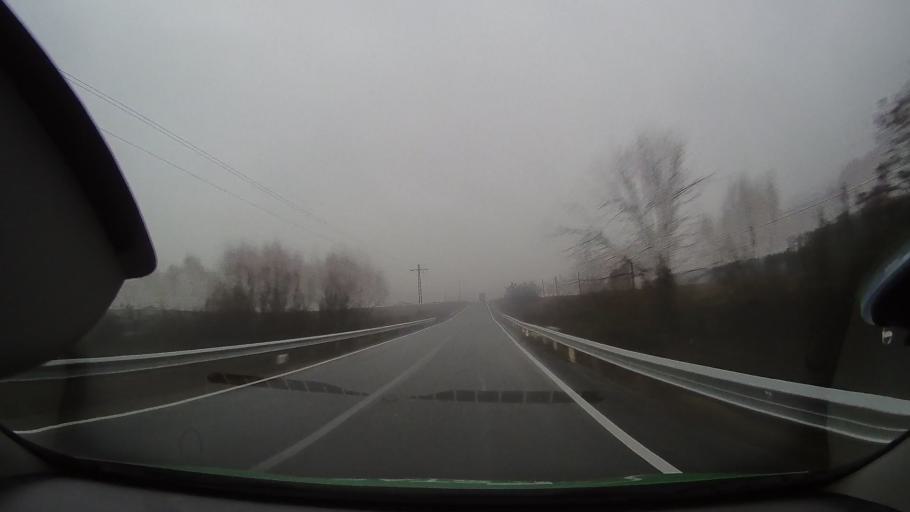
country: RO
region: Bihor
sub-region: Comuna Olcea
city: Olcea
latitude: 46.6944
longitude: 21.9650
